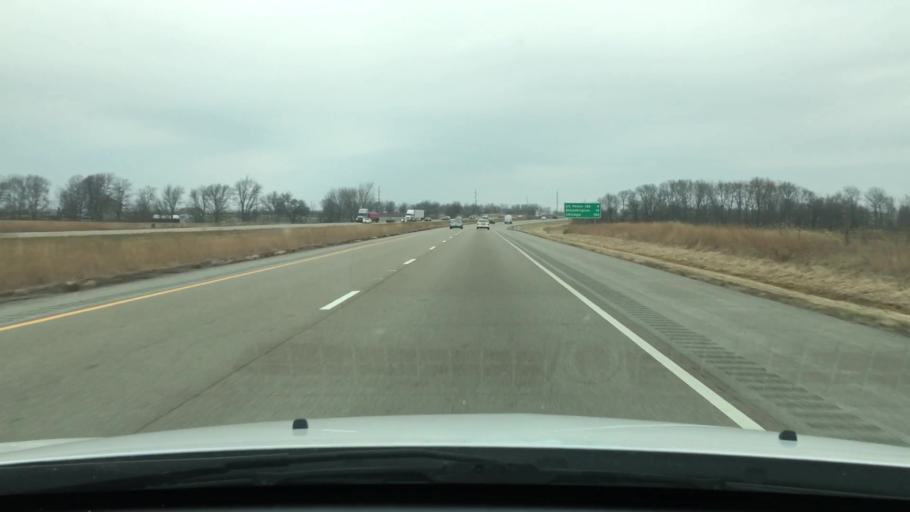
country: US
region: Illinois
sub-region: Logan County
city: Atlanta
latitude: 40.2715
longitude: -89.2127
